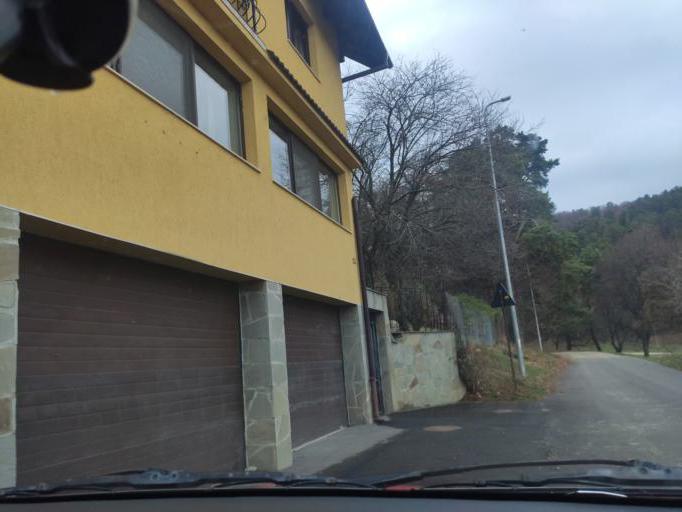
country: RO
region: Brasov
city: Codlea
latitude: 45.7053
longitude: 25.4365
